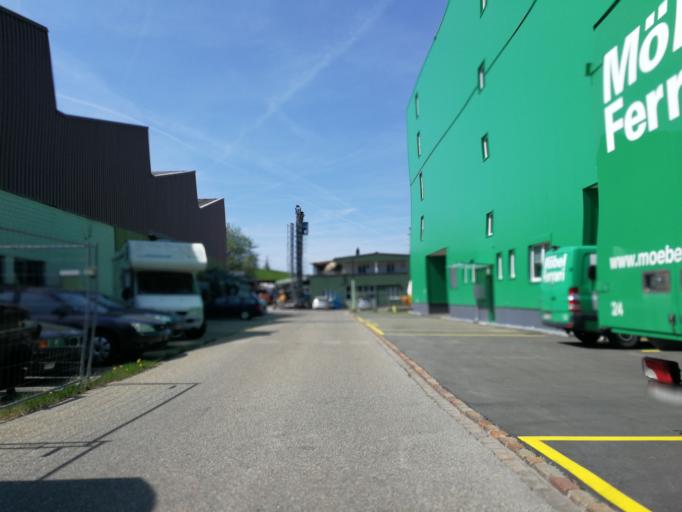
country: CH
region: Zurich
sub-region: Bezirk Hinwil
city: Hinwil
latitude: 47.3032
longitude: 8.8191
